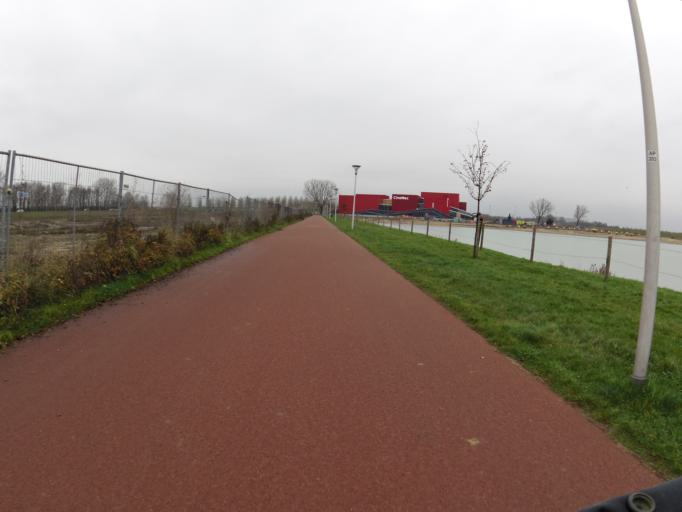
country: NL
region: Gelderland
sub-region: Gemeente Nijmegen
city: Nijmegen
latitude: 51.8769
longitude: 5.8621
